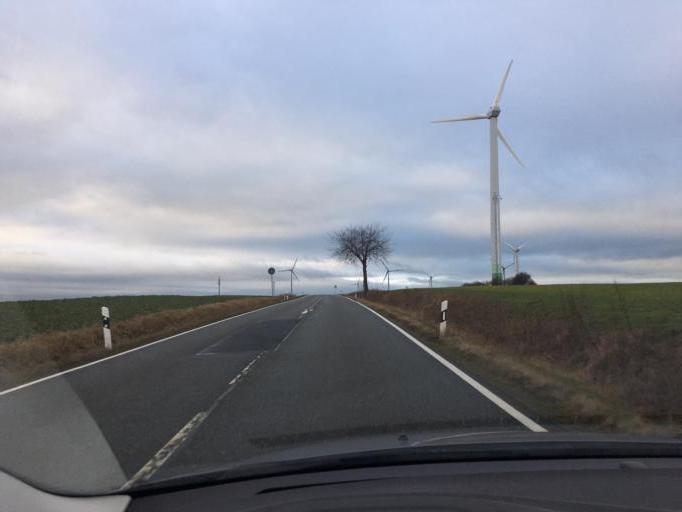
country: DE
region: Saxony
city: Penig
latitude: 50.9356
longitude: 12.6688
